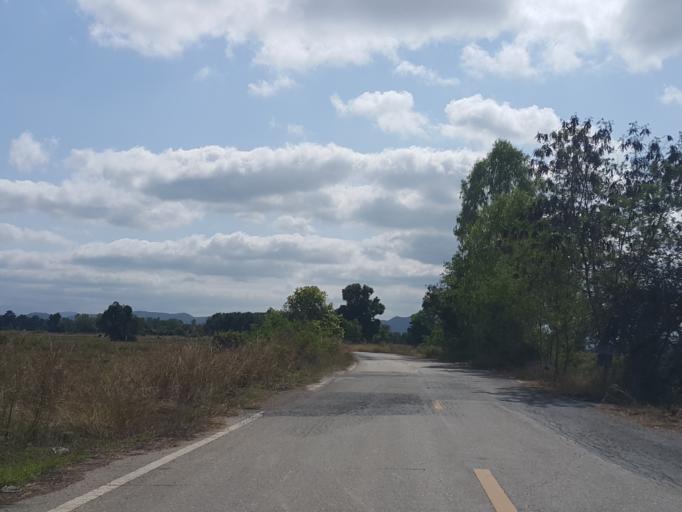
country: TH
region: Lamphun
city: Ban Thi
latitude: 18.5568
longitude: 99.0862
